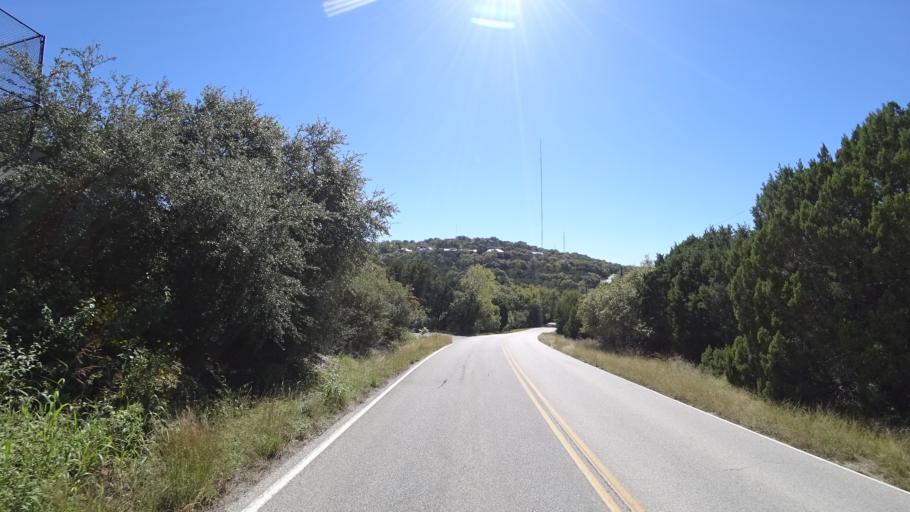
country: US
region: Texas
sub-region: Travis County
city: West Lake Hills
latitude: 30.3188
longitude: -97.7929
